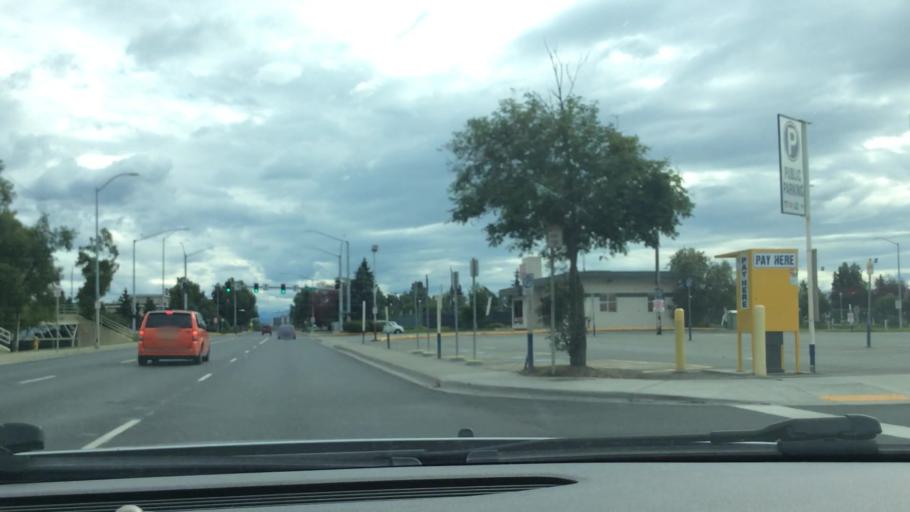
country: US
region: Alaska
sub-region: Anchorage Municipality
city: Anchorage
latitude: 61.2147
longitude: -149.8873
